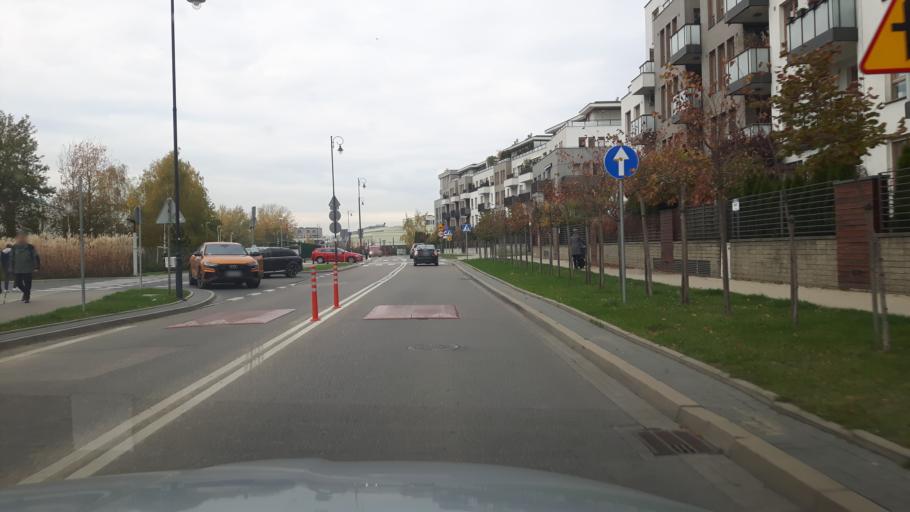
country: PL
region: Masovian Voivodeship
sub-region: Warszawa
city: Wilanow
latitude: 52.1552
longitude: 21.0707
